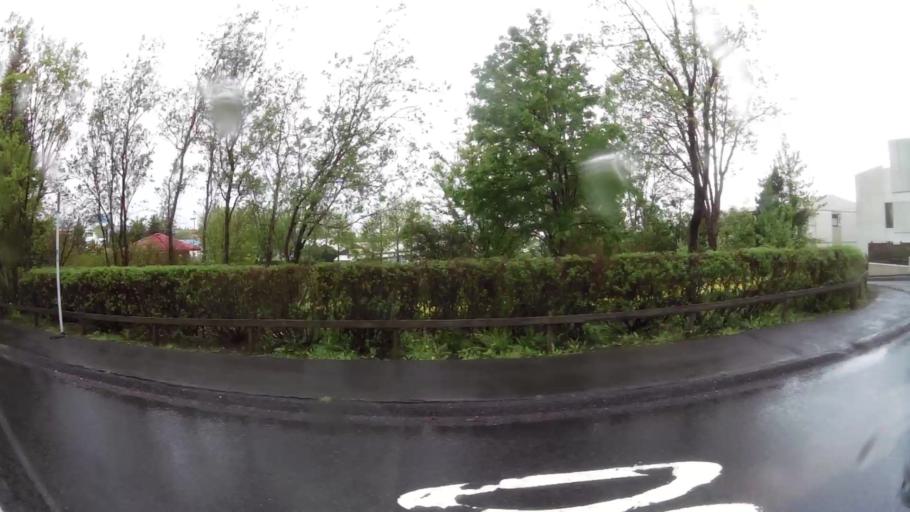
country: IS
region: Capital Region
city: Reykjavik
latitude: 64.0977
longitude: -21.8417
